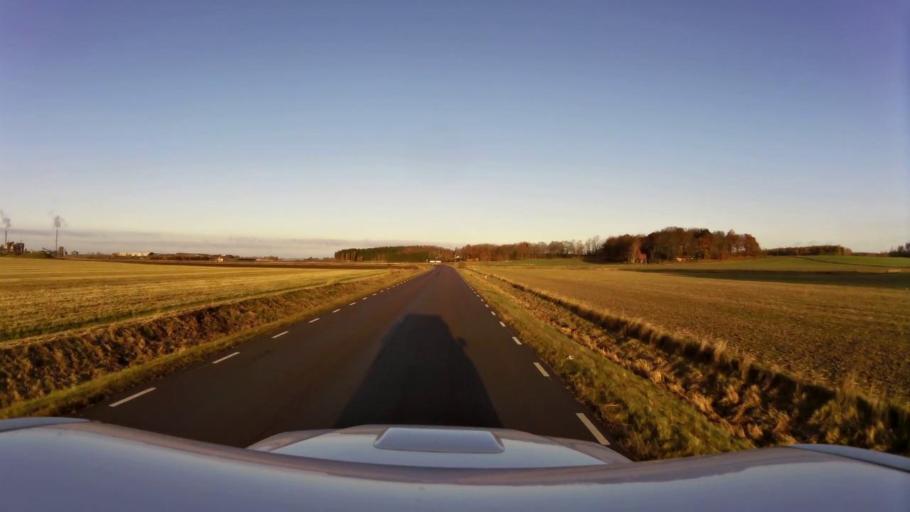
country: SE
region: OEstergoetland
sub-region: Linkopings Kommun
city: Ekangen
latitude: 58.4386
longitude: 15.6770
